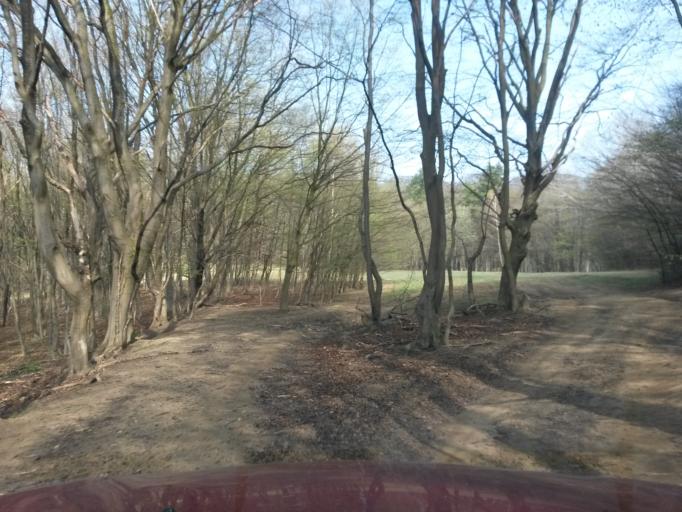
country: SK
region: Presovsky
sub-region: Okres Presov
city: Presov
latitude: 48.9243
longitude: 21.1644
